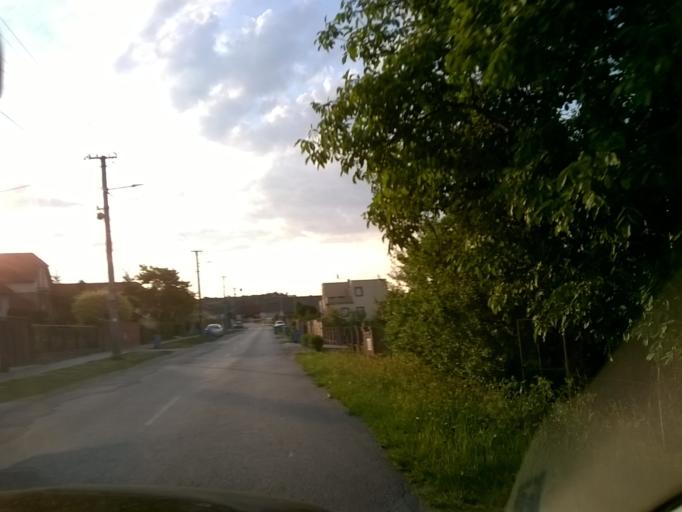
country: SK
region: Nitriansky
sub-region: Okres Nitra
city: Nitra
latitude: 48.2775
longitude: 17.9577
